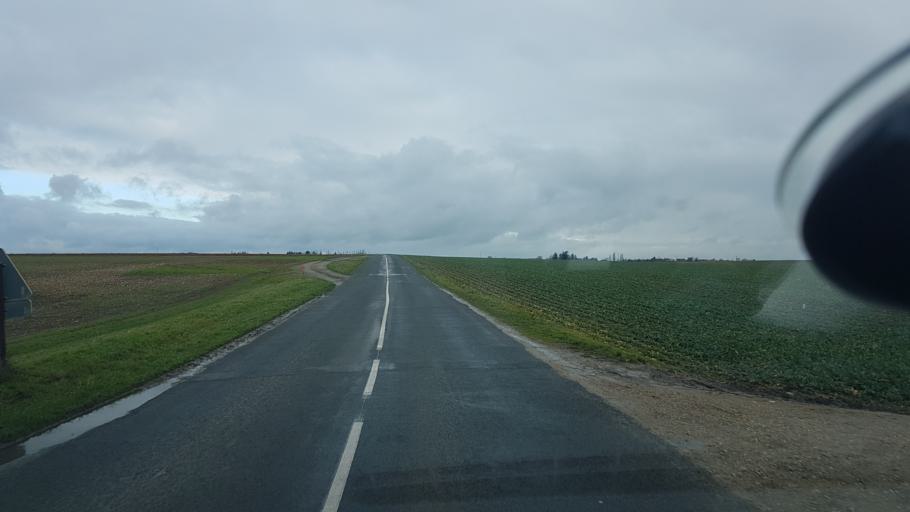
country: FR
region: Ile-de-France
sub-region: Departement de Seine-et-Marne
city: Souppes-sur-Loing
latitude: 48.2117
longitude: 2.7892
